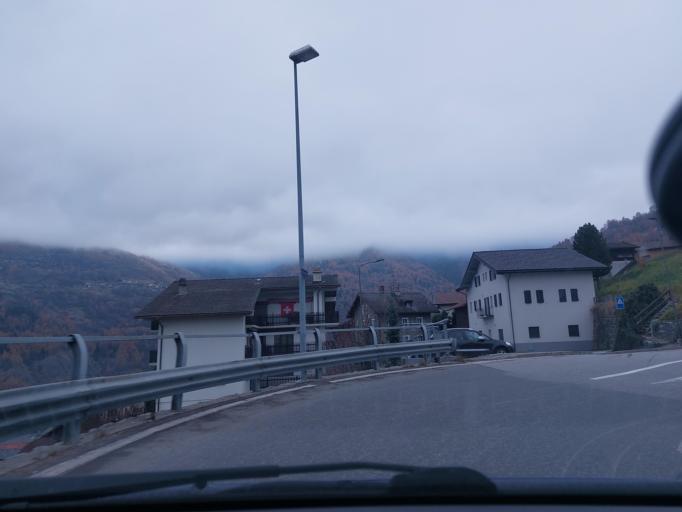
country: CH
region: Valais
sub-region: Conthey District
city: Basse-Nendaz
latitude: 46.1917
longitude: 7.3098
